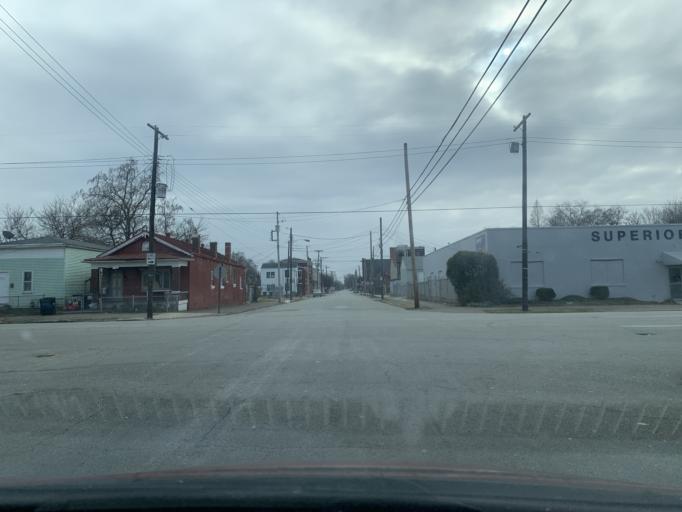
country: US
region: Kentucky
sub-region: Jefferson County
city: Louisville
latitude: 38.2596
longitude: -85.7814
